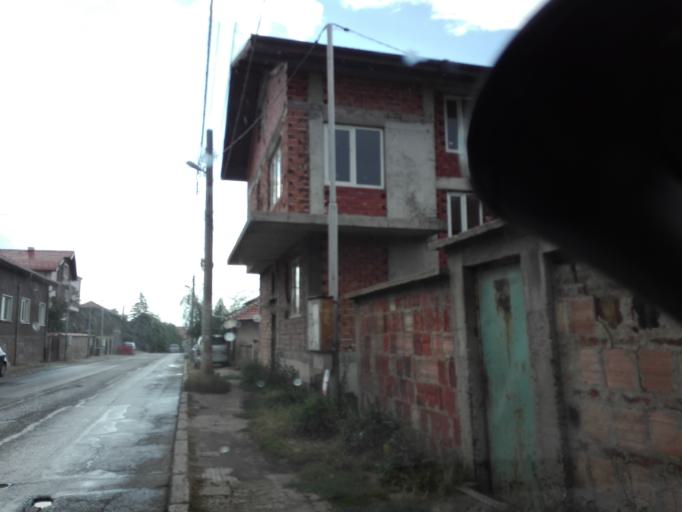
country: BG
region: Sofiya
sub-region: Obshtina Elin Pelin
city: Elin Pelin
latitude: 42.6025
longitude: 23.4777
